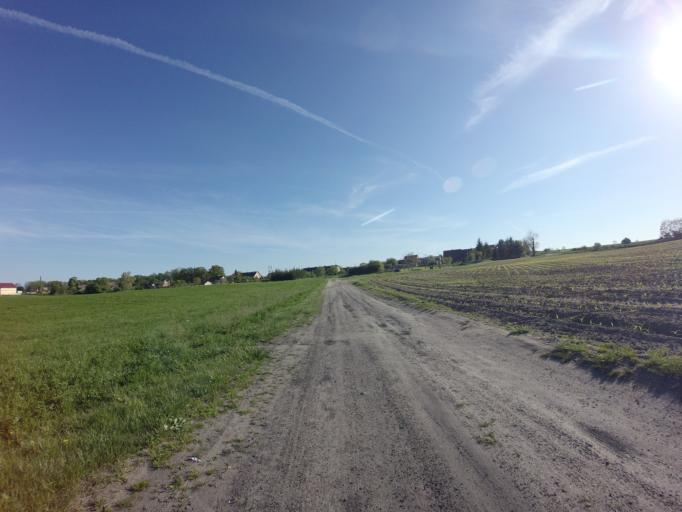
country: PL
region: West Pomeranian Voivodeship
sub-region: Powiat choszczenski
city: Pelczyce
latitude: 53.1213
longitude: 15.3219
